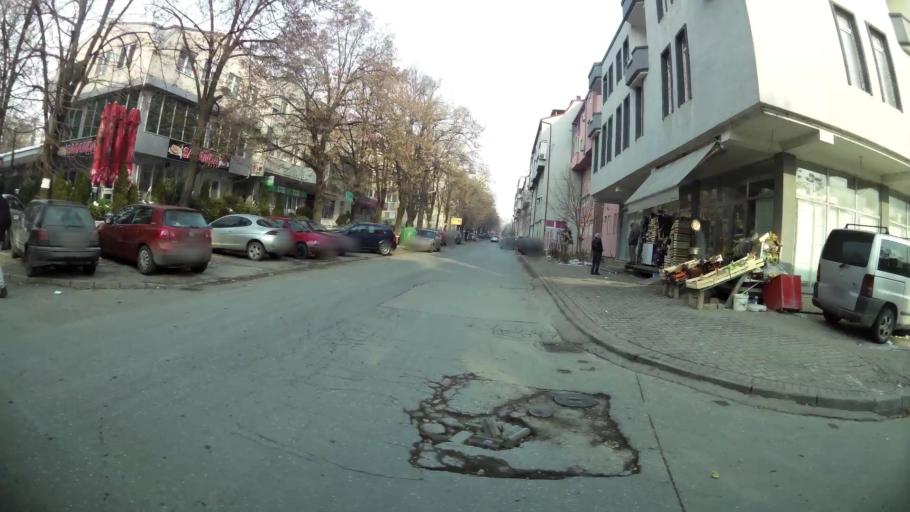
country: MK
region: Cair
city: Cair
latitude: 42.0157
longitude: 21.4348
